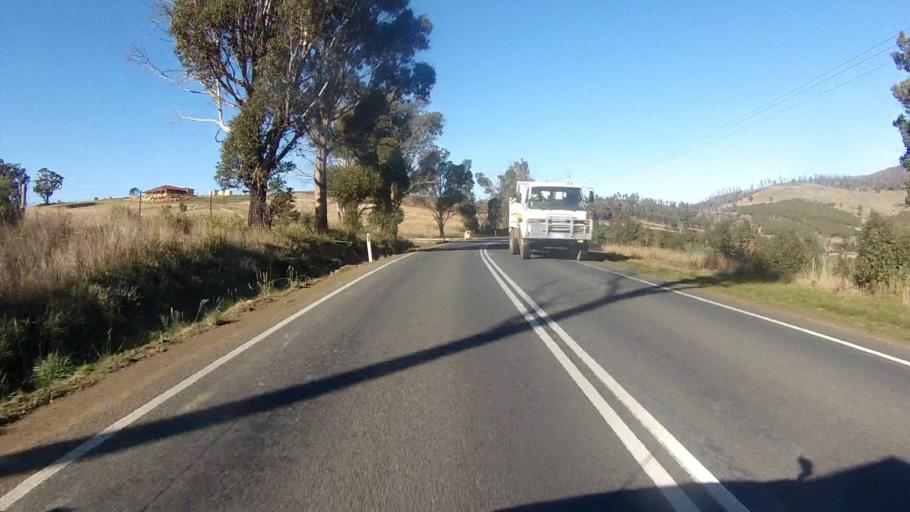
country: AU
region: Tasmania
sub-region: Sorell
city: Sorell
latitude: -42.8335
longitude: 147.8068
